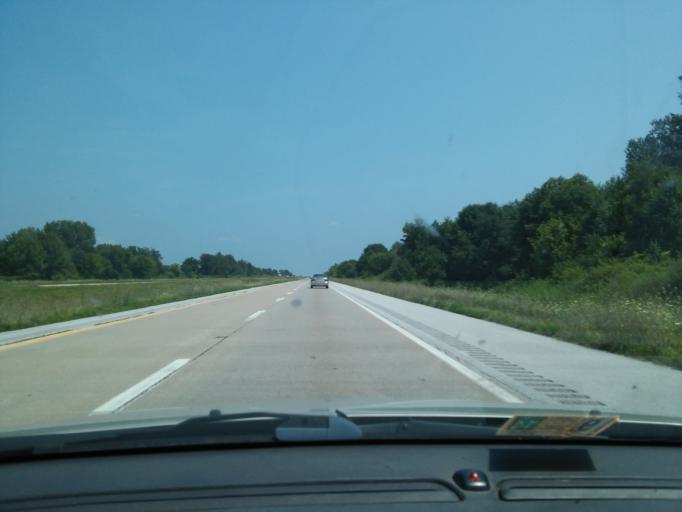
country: US
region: Illinois
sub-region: Scott County
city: Winchester
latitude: 39.6810
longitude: -90.4997
